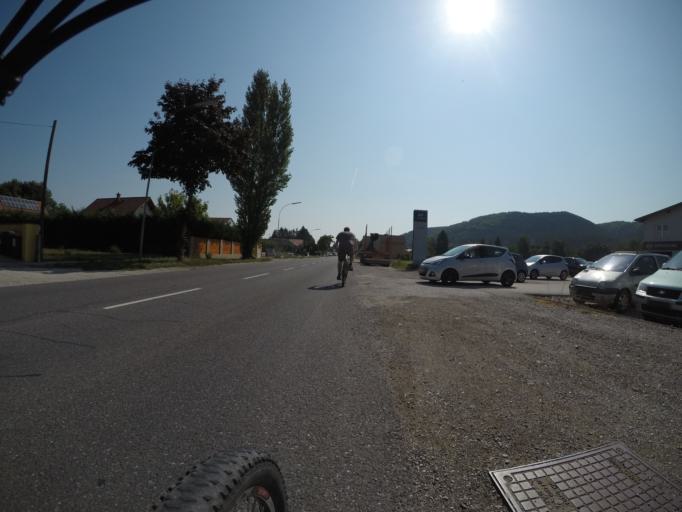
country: AT
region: Lower Austria
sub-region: Politischer Bezirk Baden
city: Hirtenberg
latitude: 47.9375
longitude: 16.1476
